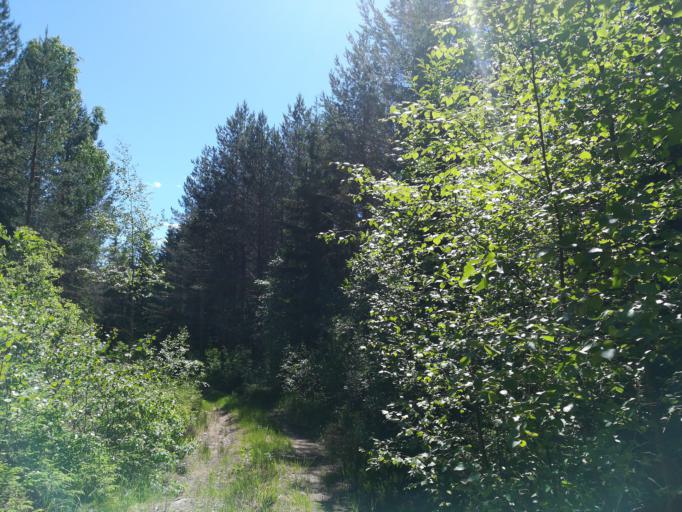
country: FI
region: Southern Savonia
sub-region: Mikkeli
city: Puumala
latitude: 61.6176
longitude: 28.1614
